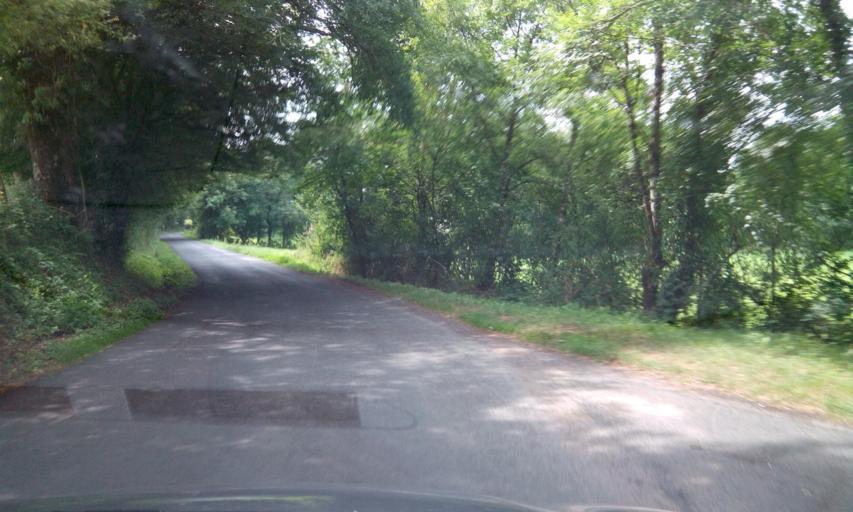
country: FR
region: Limousin
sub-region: Departement de la Correze
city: Meyssac
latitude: 45.0466
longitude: 1.6203
